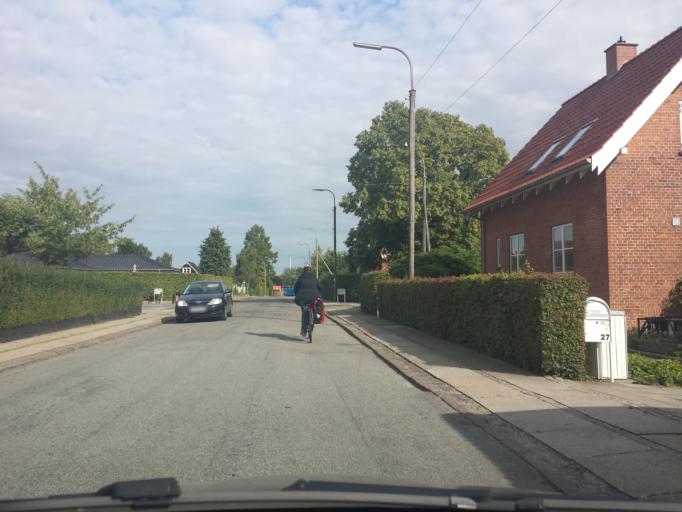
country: DK
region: Capital Region
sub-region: Ballerup Kommune
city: Ballerup
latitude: 55.7254
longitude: 12.4013
